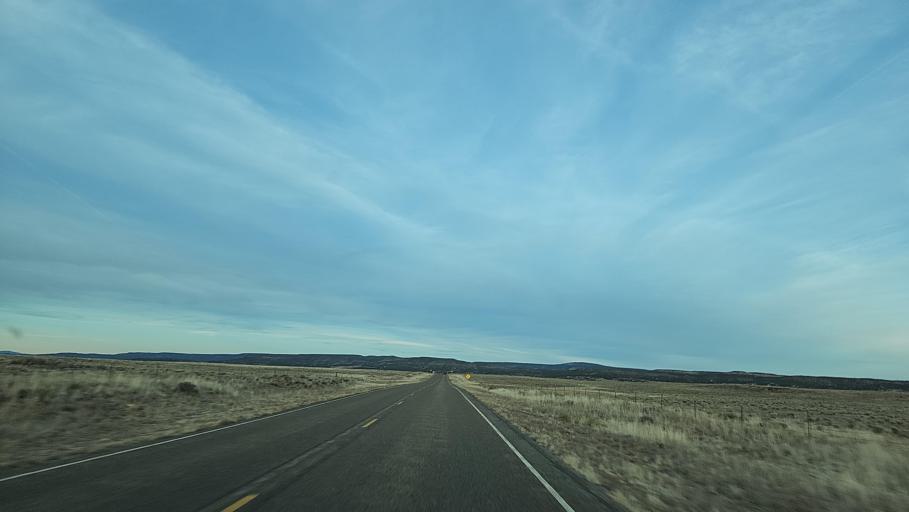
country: US
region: New Mexico
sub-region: Cibola County
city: Grants
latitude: 34.7016
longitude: -108.0323
